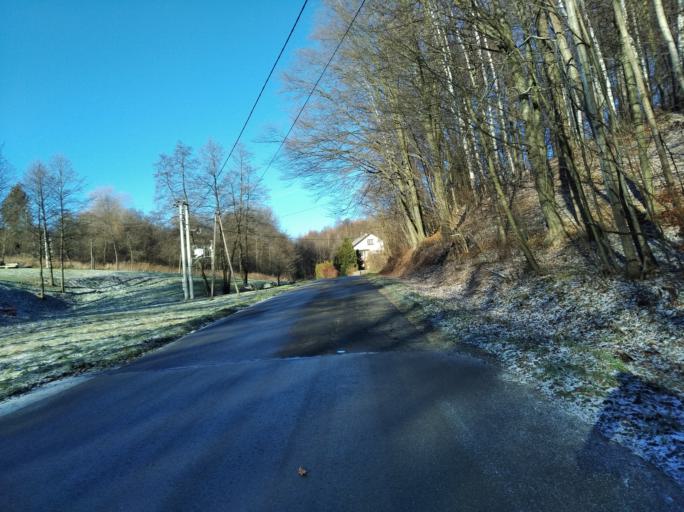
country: PL
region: Subcarpathian Voivodeship
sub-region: Powiat ropczycko-sedziszowski
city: Iwierzyce
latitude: 49.9626
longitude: 21.7572
